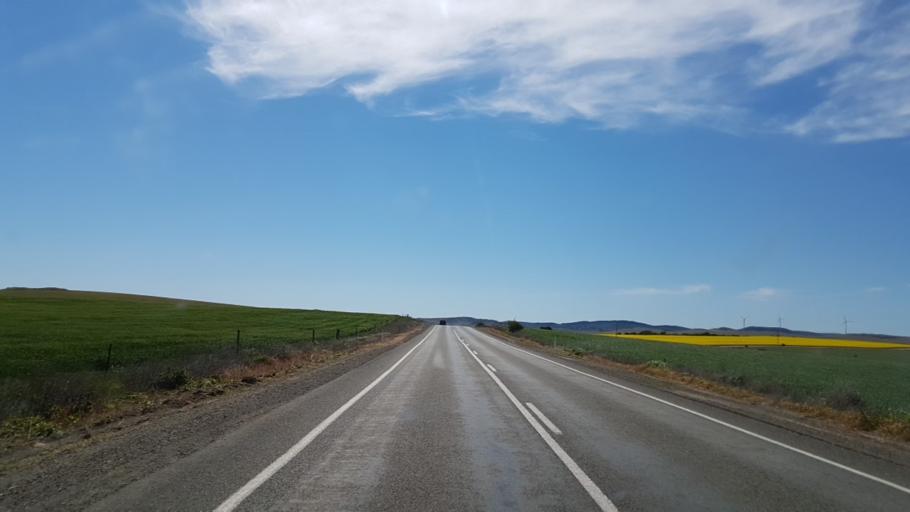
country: AU
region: South Australia
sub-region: Clare and Gilbert Valleys
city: Clare
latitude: -33.9245
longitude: 138.8614
